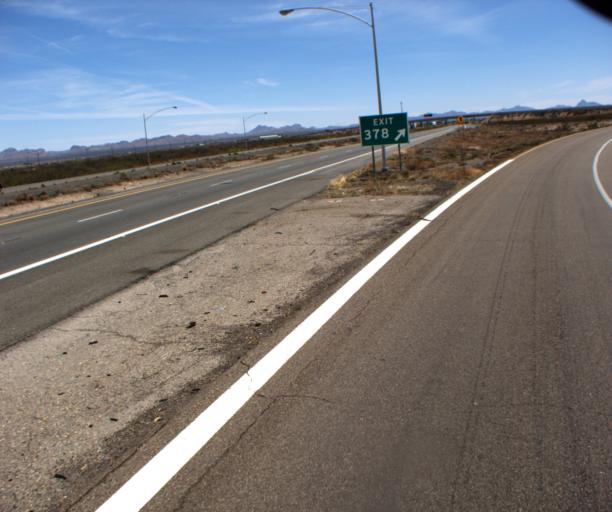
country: US
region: New Mexico
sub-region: Hidalgo County
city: Lordsburg
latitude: 32.2739
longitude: -109.2549
